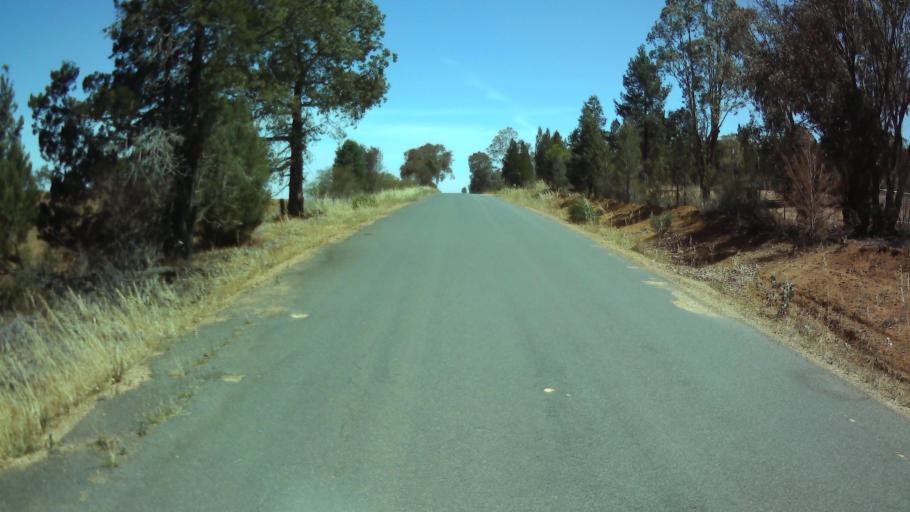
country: AU
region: New South Wales
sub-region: Weddin
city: Grenfell
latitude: -33.9027
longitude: 148.1836
